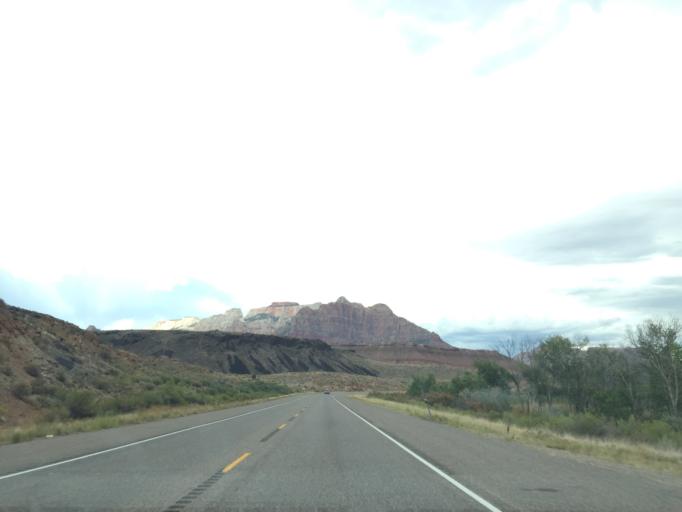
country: US
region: Utah
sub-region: Washington County
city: LaVerkin
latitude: 37.1703
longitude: -113.0951
